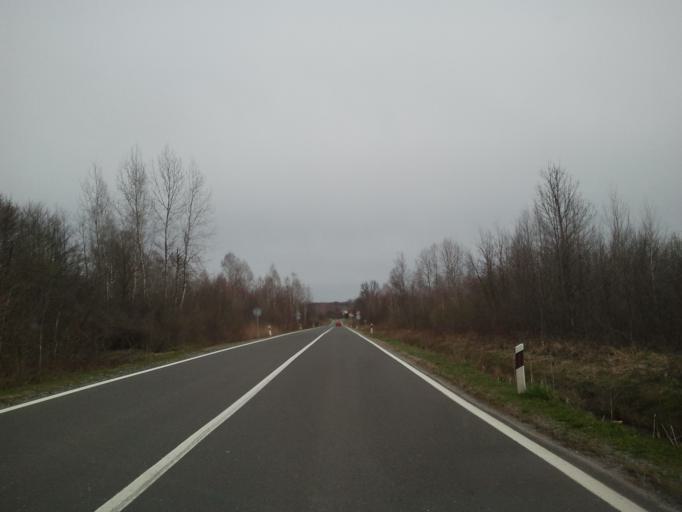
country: HR
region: Sisacko-Moslavacka
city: Gvozd
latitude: 45.3278
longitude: 15.9710
